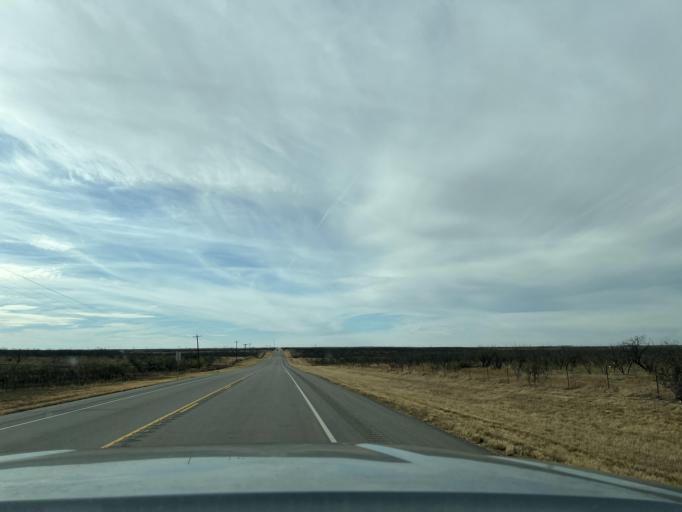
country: US
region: Texas
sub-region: Jones County
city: Anson
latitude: 32.7507
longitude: -99.6897
